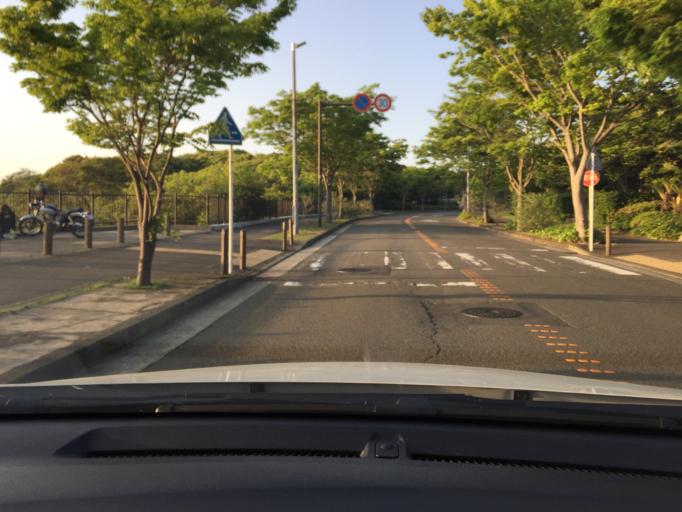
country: JP
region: Kanagawa
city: Hayama
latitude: 35.2591
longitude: 139.6066
